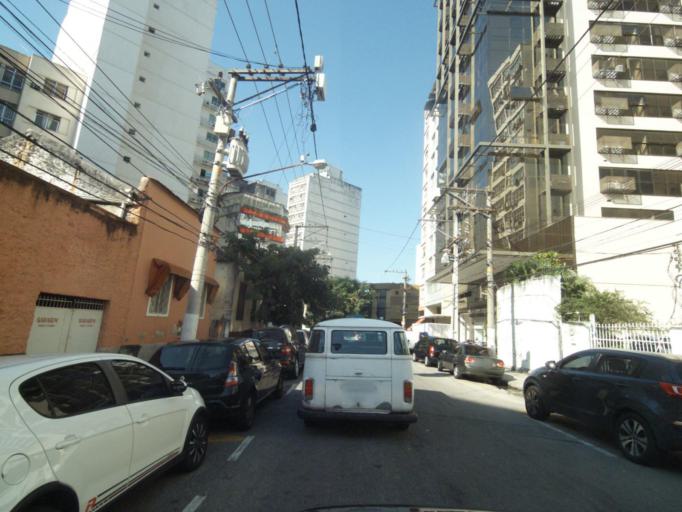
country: BR
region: Rio de Janeiro
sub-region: Niteroi
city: Niteroi
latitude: -22.8970
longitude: -43.1218
